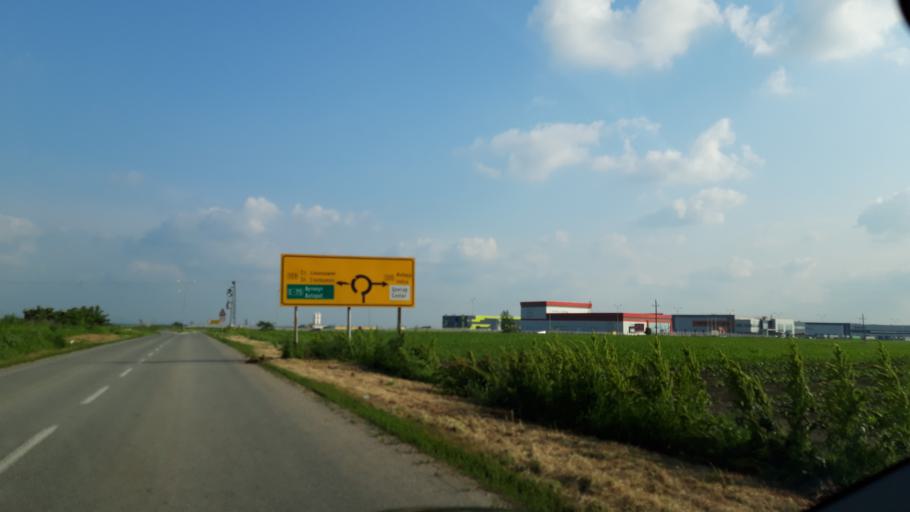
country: RS
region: Autonomna Pokrajina Vojvodina
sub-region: Sremski Okrug
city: Ingija
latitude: 45.0662
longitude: 20.1275
